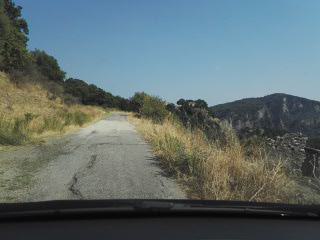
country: IT
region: Calabria
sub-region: Provincia di Reggio Calabria
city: Camini
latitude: 38.4474
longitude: 16.4665
